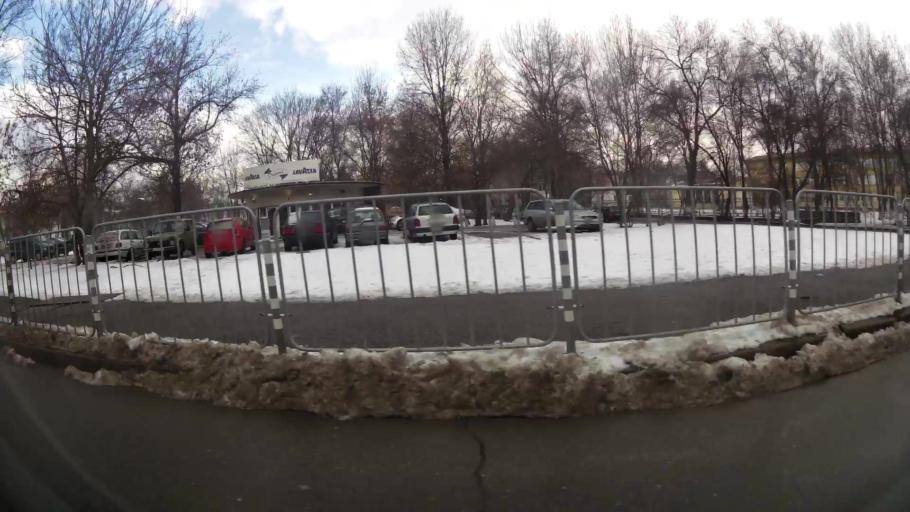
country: BG
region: Sofia-Capital
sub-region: Stolichna Obshtina
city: Sofia
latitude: 42.7042
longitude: 23.2831
